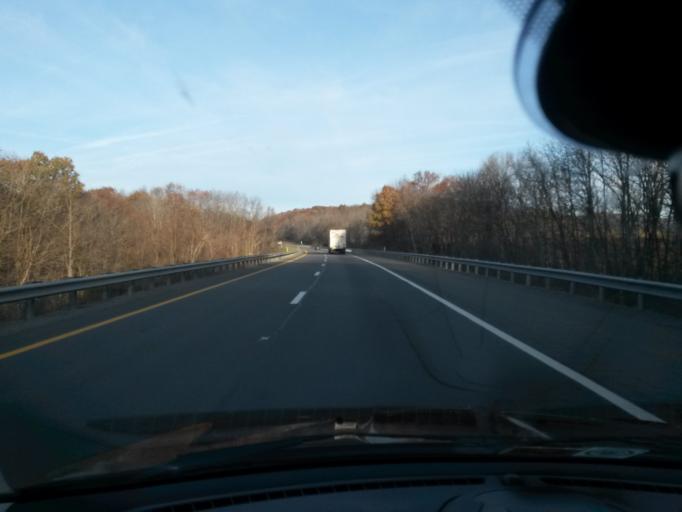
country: US
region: West Virginia
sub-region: Greenbrier County
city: Lewisburg
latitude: 37.8260
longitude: -80.4451
